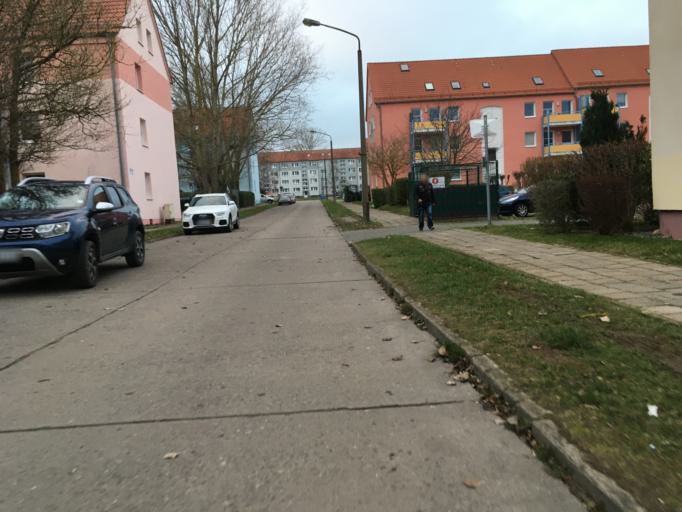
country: DE
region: Mecklenburg-Vorpommern
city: Sassnitz
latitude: 54.5104
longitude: 13.6251
